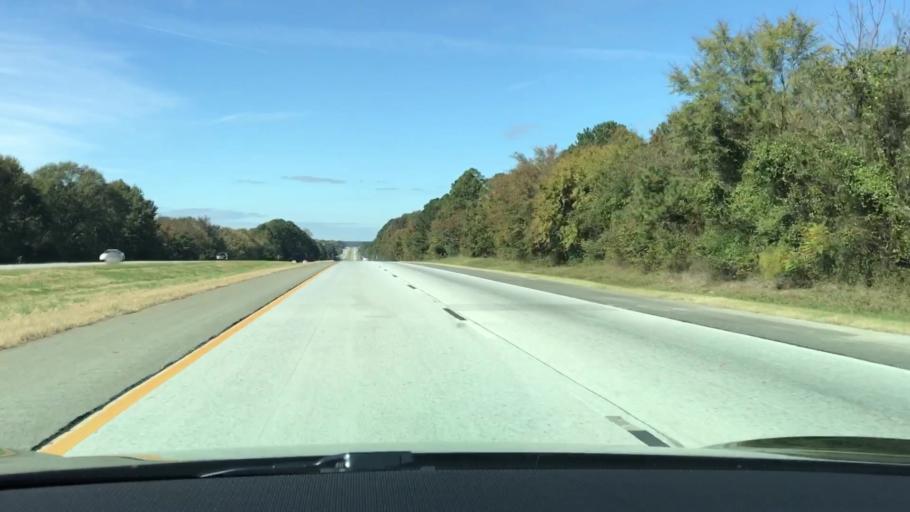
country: US
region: Georgia
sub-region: Putnam County
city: Jefferson
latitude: 33.5427
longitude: -83.3243
